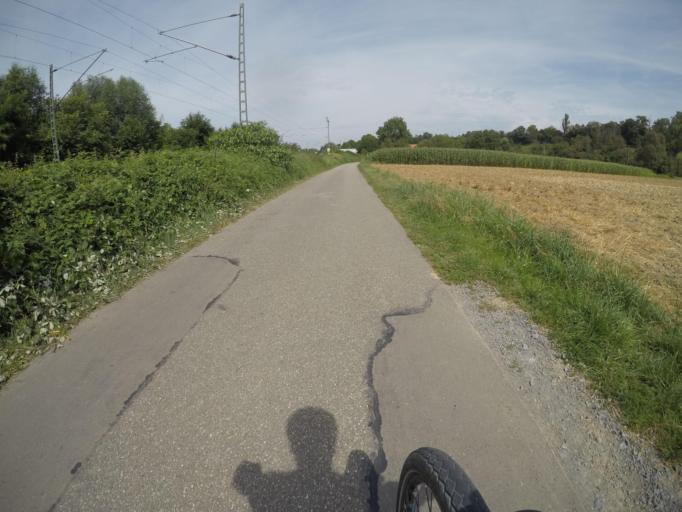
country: DE
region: Baden-Wuerttemberg
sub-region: Karlsruhe Region
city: Gondelsheim
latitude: 49.0843
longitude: 8.6520
